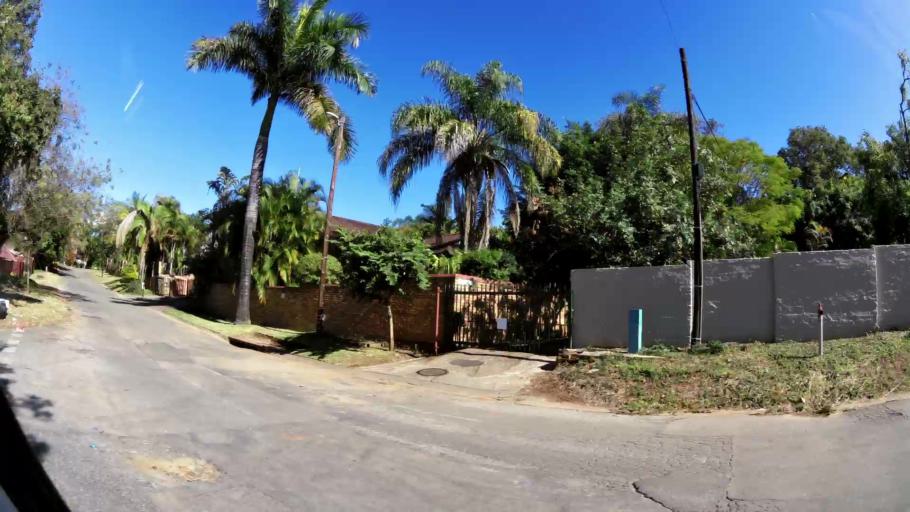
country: ZA
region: Limpopo
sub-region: Mopani District Municipality
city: Tzaneen
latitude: -23.8283
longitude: 30.1475
